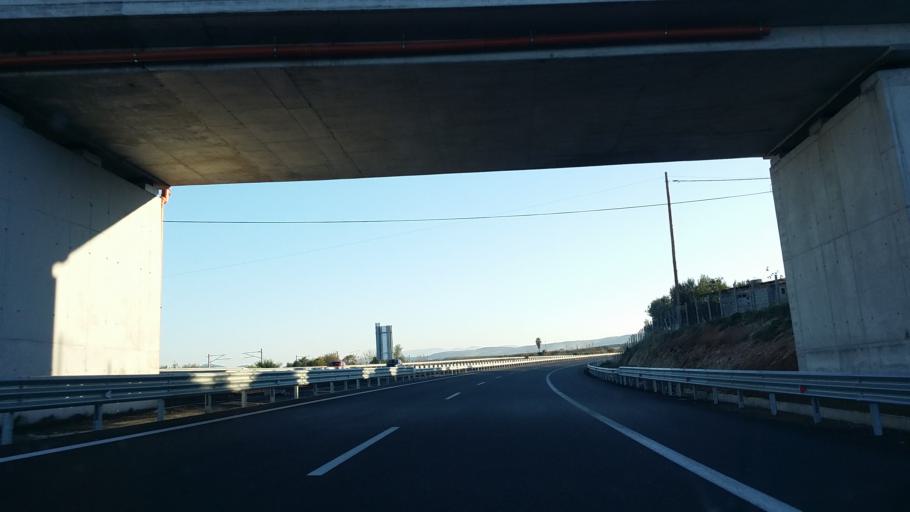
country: GR
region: Peloponnese
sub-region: Nomos Korinthias
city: Velo
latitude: 37.9669
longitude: 22.7481
